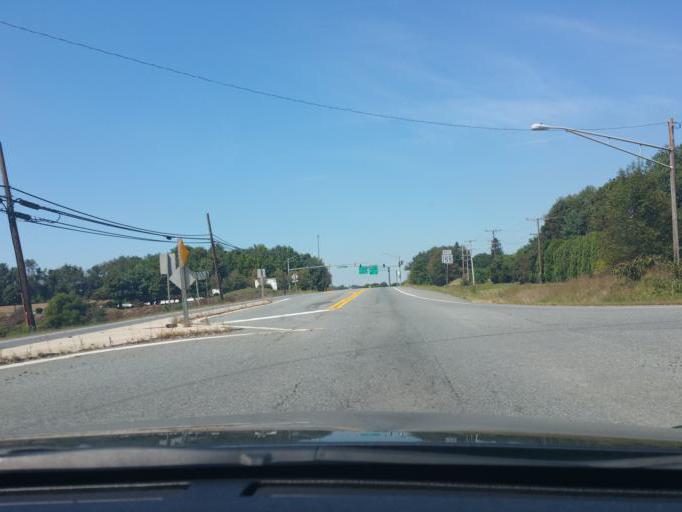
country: US
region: Maryland
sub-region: Harford County
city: Havre de Grace
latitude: 39.5672
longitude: -76.1292
